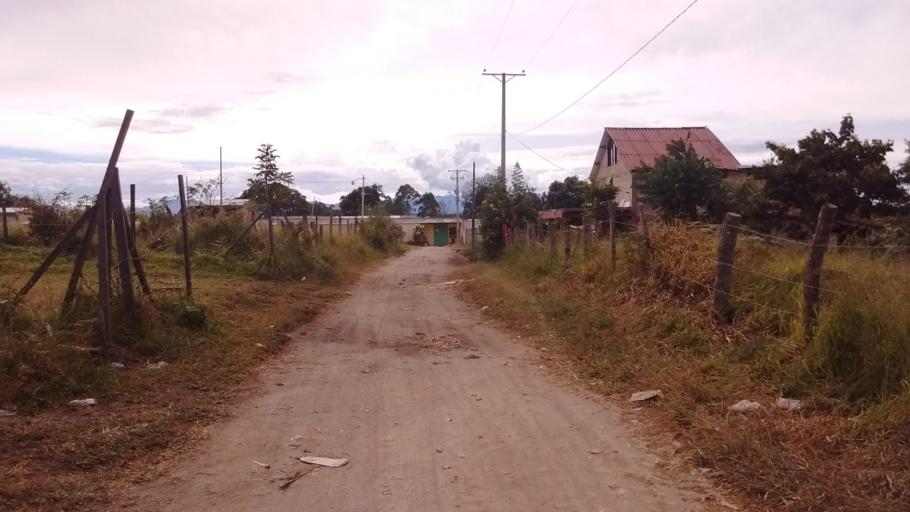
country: CO
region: Cauca
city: Popayan
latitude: 2.4922
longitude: -76.5846
